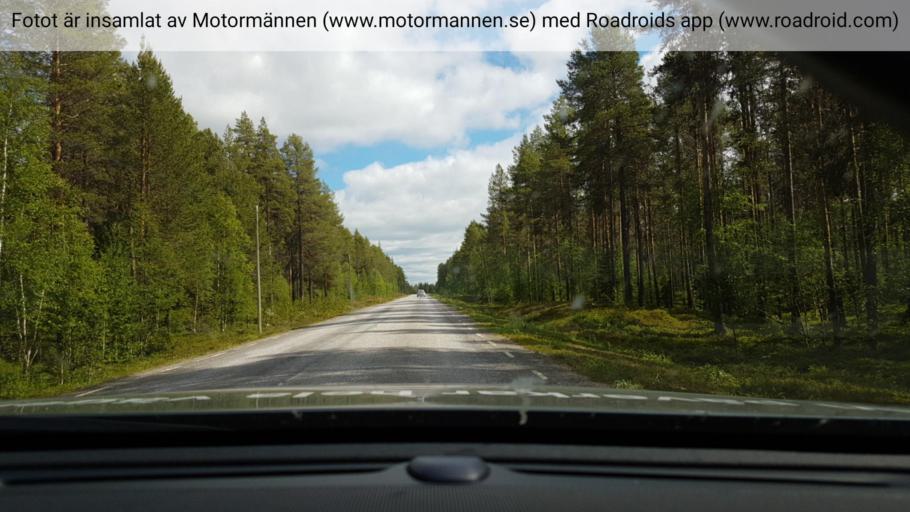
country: SE
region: Vaesterbotten
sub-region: Sorsele Kommun
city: Sorsele
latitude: 65.6837
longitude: 17.3444
